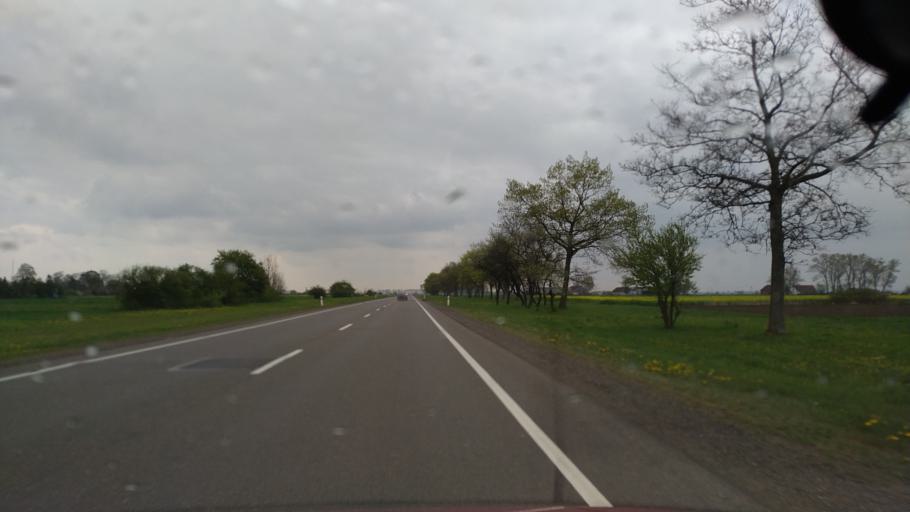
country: PL
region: Pomeranian Voivodeship
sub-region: Powiat malborski
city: Lisewo Malborskie
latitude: 54.0550
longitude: 18.8636
